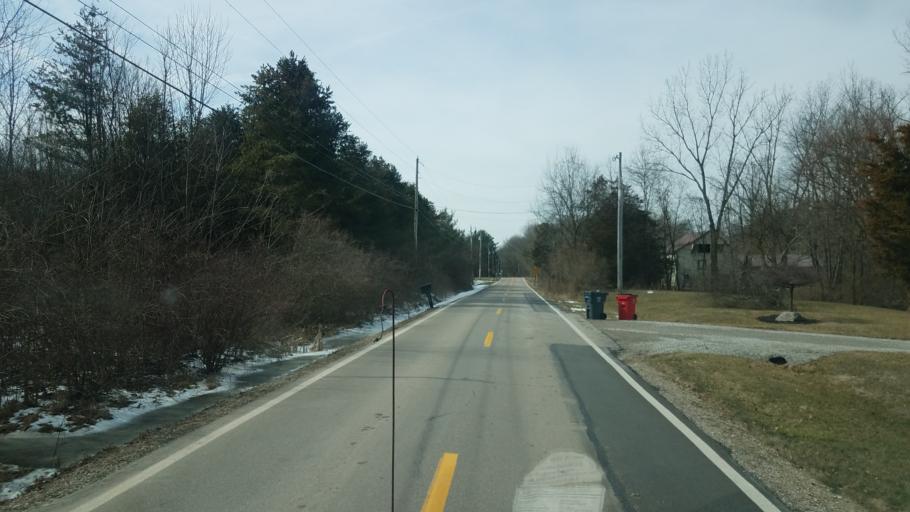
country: US
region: Ohio
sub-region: Delaware County
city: Sunbury
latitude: 40.2849
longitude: -82.9319
